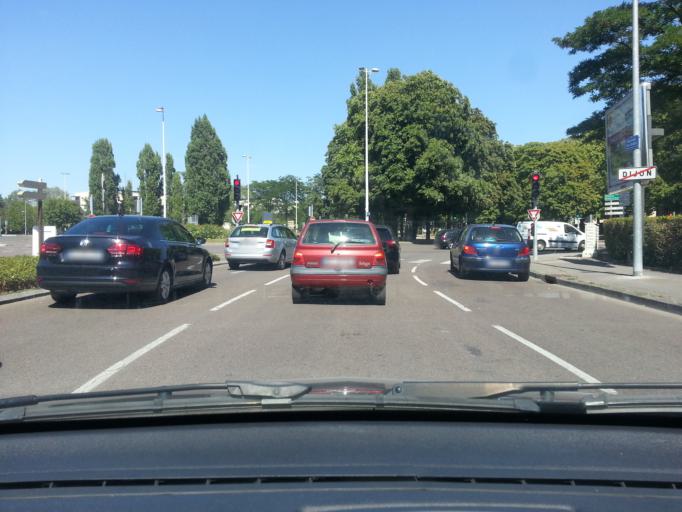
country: FR
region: Bourgogne
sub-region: Departement de la Cote-d'Or
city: Saint-Apollinaire
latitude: 47.3284
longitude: 5.0697
